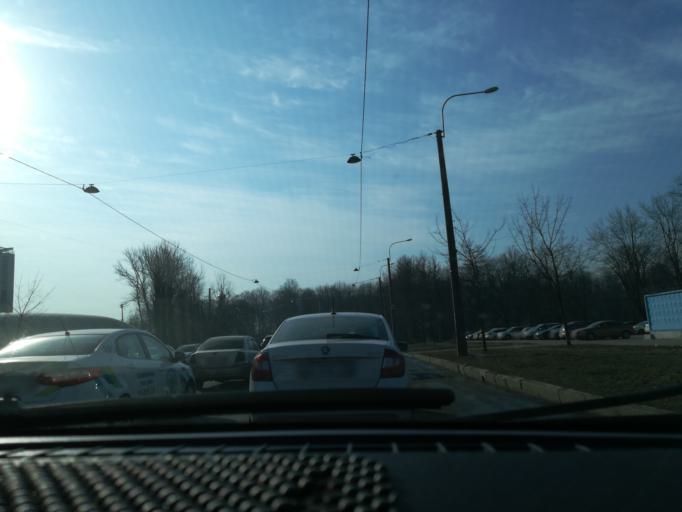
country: RU
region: St.-Petersburg
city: Vasyl'evsky Ostrov
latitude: 59.9488
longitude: 30.2488
